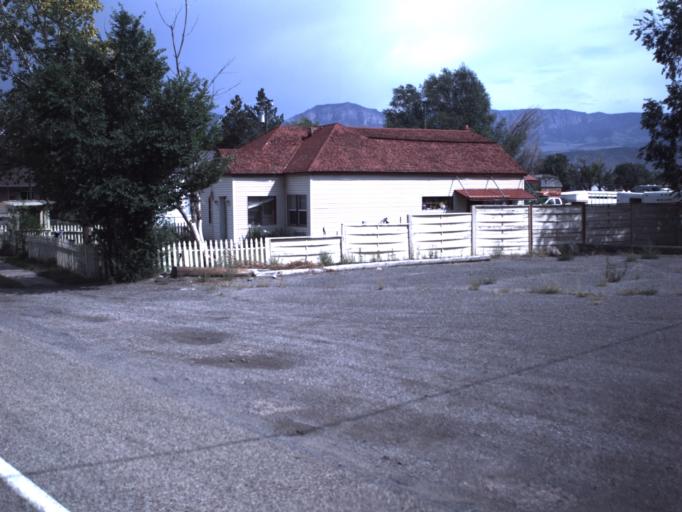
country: US
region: Utah
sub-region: Piute County
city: Junction
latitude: 38.1717
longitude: -112.2766
